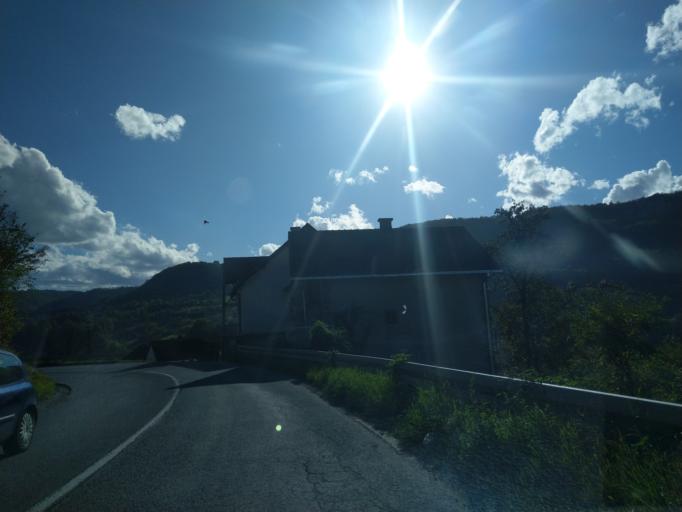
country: RS
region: Central Serbia
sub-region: Zlatiborski Okrug
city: Uzice
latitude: 43.8640
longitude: 19.8141
